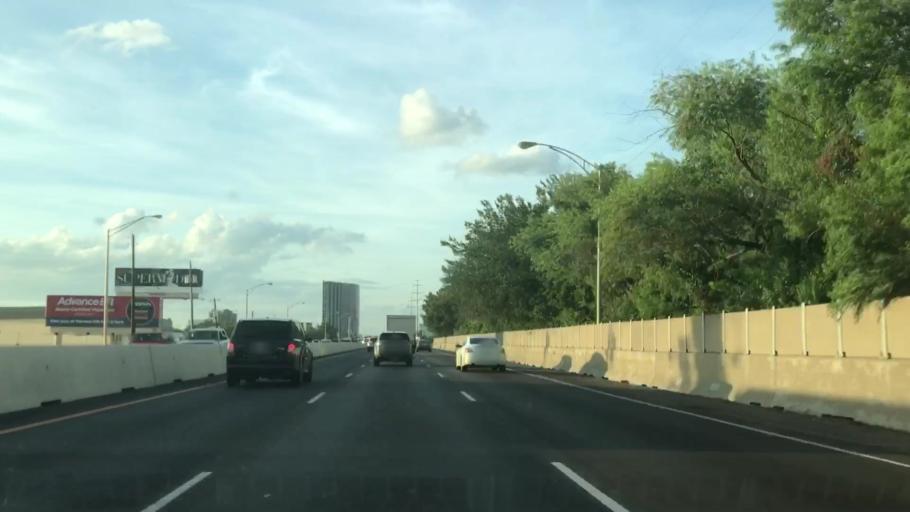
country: US
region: Texas
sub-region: Dallas County
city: Addison
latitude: 32.9159
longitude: -96.8167
